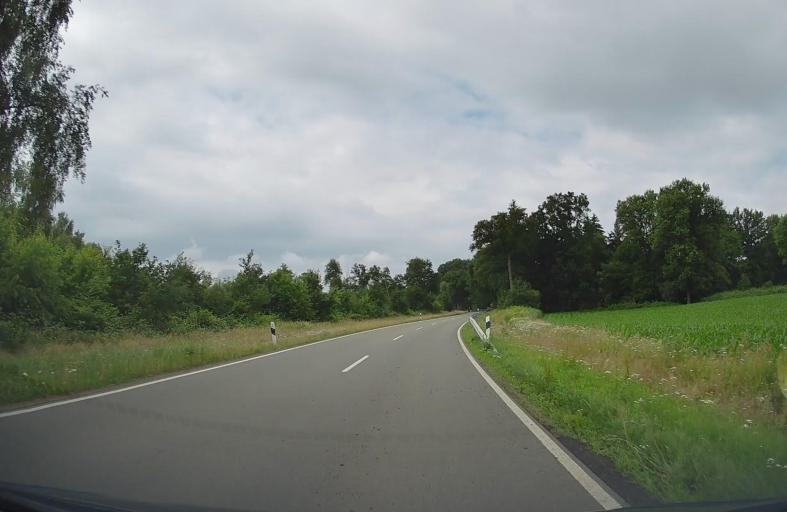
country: DE
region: Lower Saxony
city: Friesoythe
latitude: 53.0404
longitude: 7.8328
